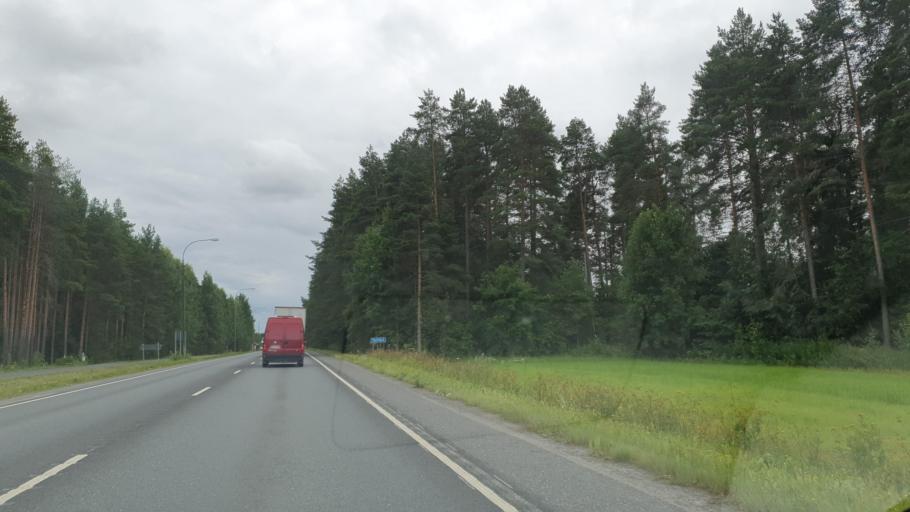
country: FI
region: Northern Savo
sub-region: Ylae-Savo
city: Lapinlahti
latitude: 63.4678
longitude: 27.3061
